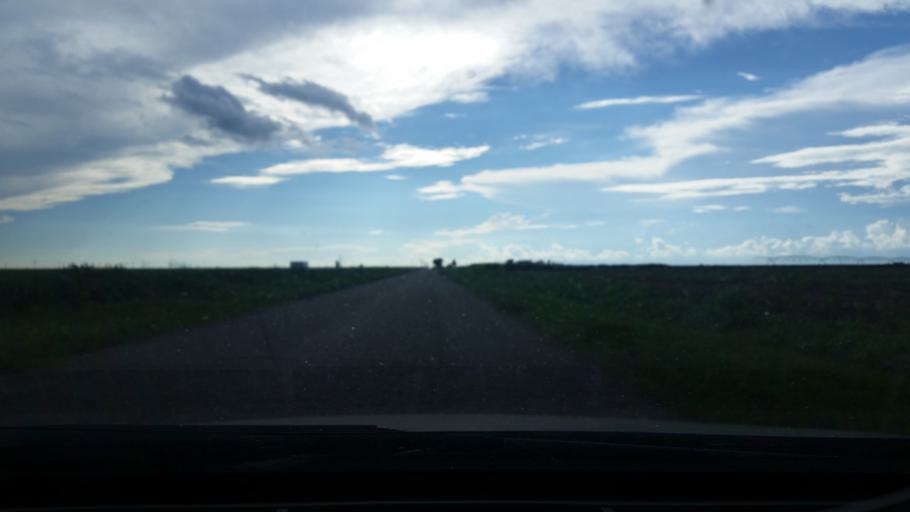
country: US
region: New Mexico
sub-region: Curry County
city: Clovis
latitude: 34.4630
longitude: -103.2211
